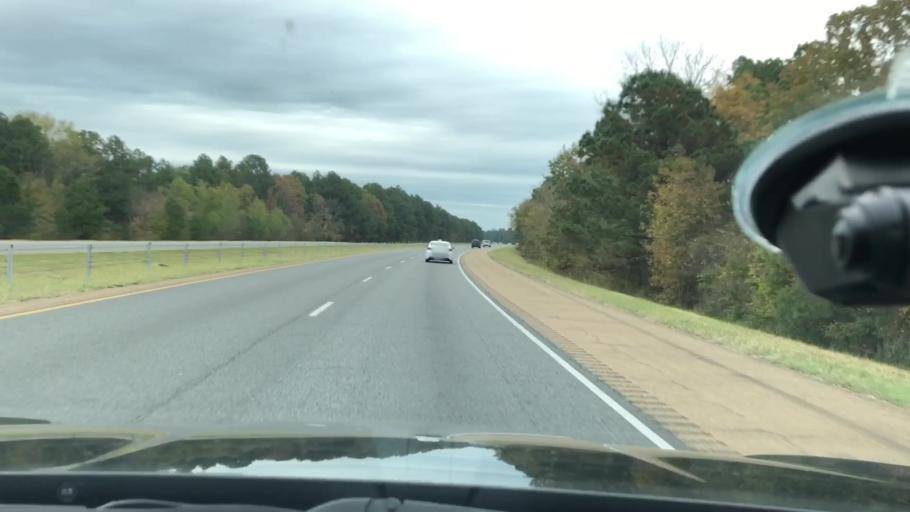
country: US
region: Arkansas
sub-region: Clark County
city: Gurdon
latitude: 33.9522
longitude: -93.2318
